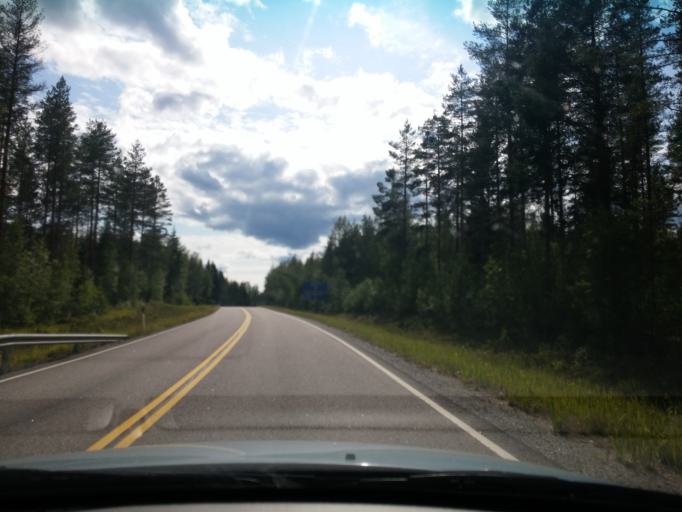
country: FI
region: Central Finland
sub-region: Saarijaervi-Viitasaari
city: Pylkoenmaeki
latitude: 62.5921
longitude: 24.5987
